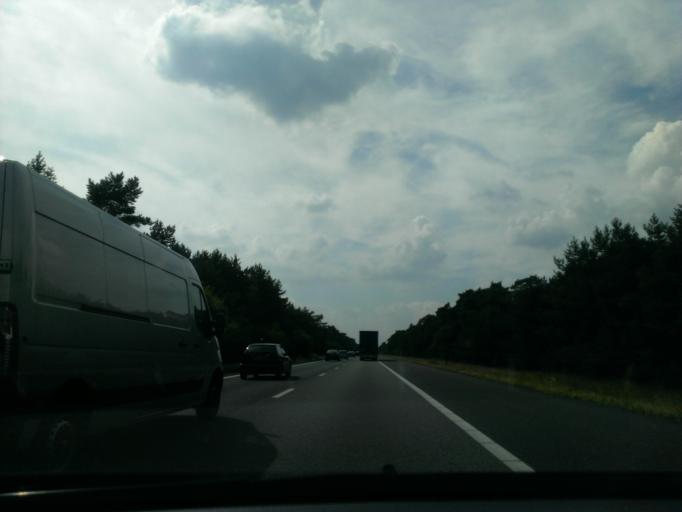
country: NL
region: Gelderland
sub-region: Gemeente Barneveld
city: Garderen
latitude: 52.1963
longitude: 5.7506
